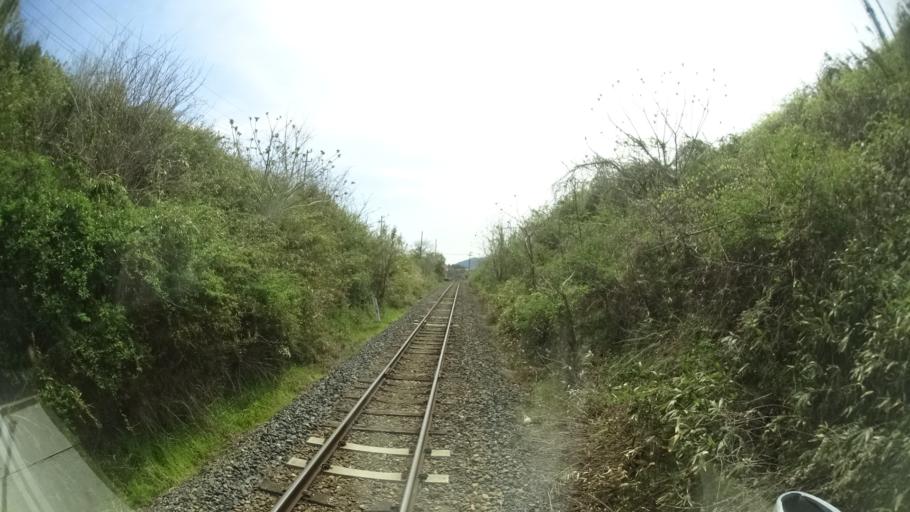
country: JP
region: Iwate
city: Ichinoseki
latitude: 38.9975
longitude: 141.2714
